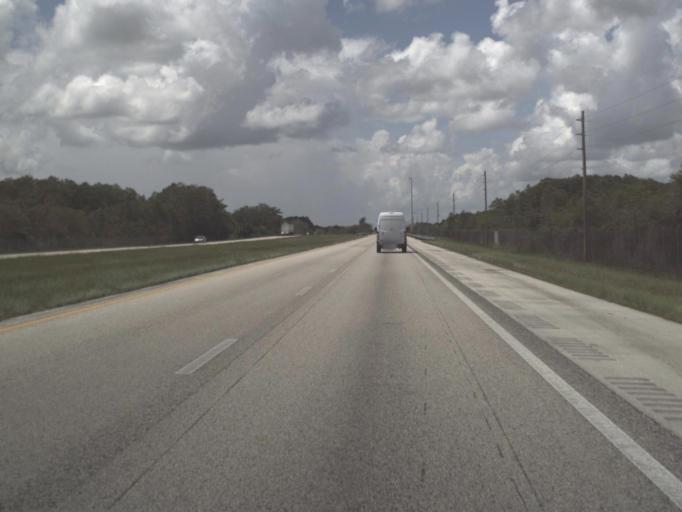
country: US
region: Florida
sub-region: Broward County
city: Weston
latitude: 26.1720
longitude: -80.9207
